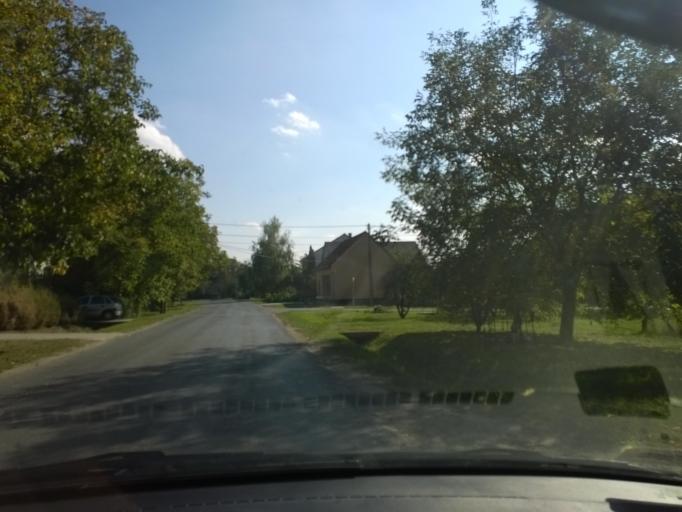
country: HU
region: Bacs-Kiskun
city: Kalocsa
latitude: 46.4883
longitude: 19.0717
